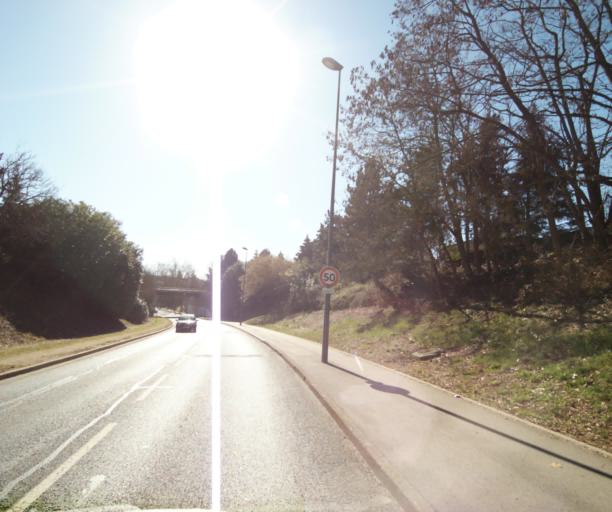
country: FR
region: Lorraine
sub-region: Departement de Meurthe-et-Moselle
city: Heillecourt
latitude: 48.6586
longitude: 6.1988
